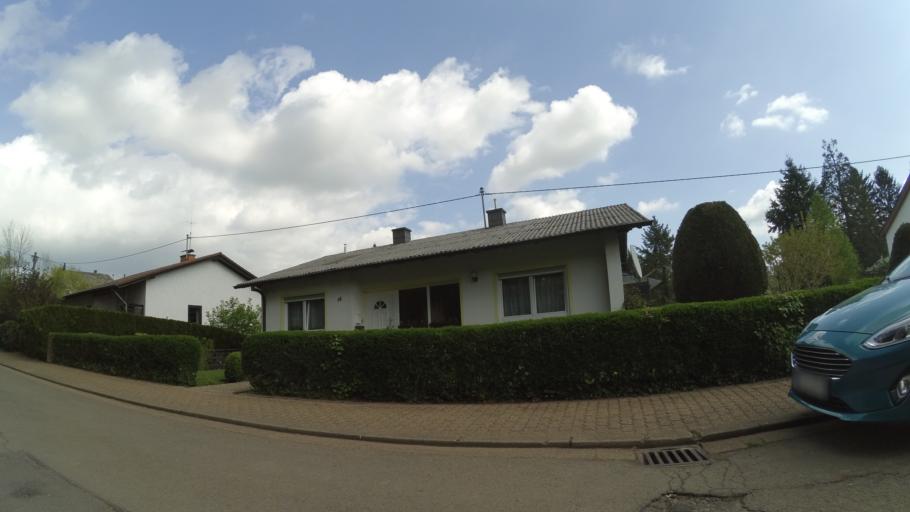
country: DE
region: Saarland
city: Wadern
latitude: 49.5367
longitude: 6.8857
